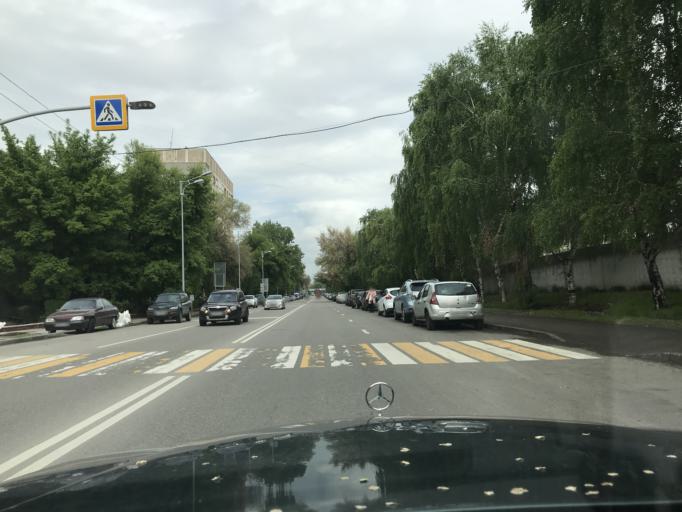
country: KZ
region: Almaty Qalasy
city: Almaty
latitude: 43.2049
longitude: 76.8710
